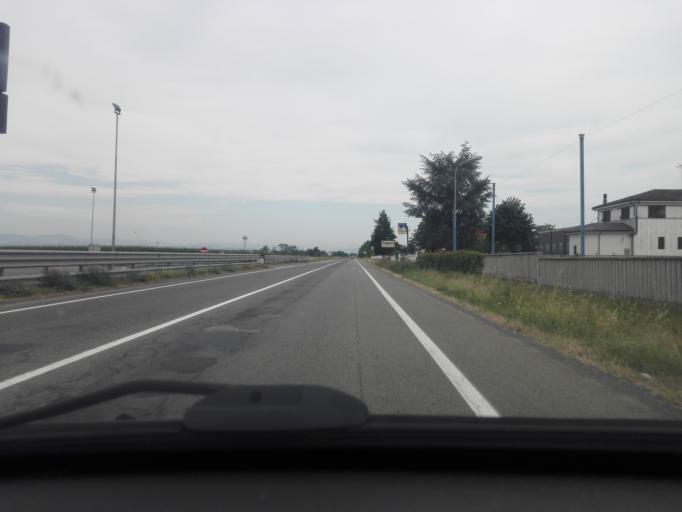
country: IT
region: Piedmont
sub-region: Provincia di Alessandria
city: Mandrogne
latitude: 44.8347
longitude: 8.7369
